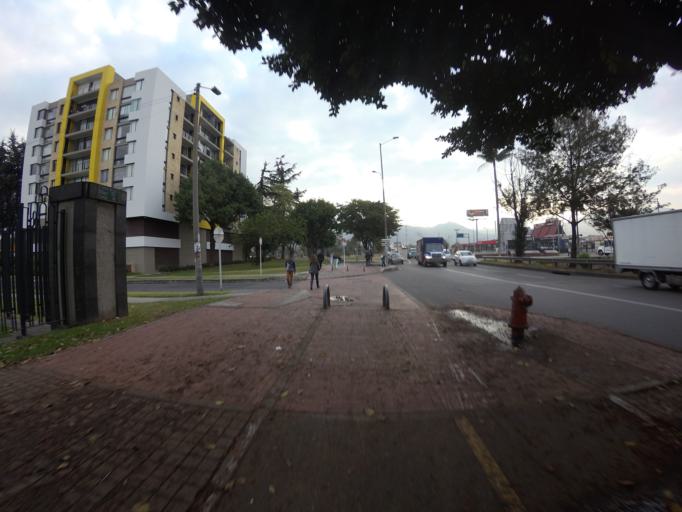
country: CO
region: Bogota D.C.
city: Barrio San Luis
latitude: 4.7075
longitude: -74.0560
